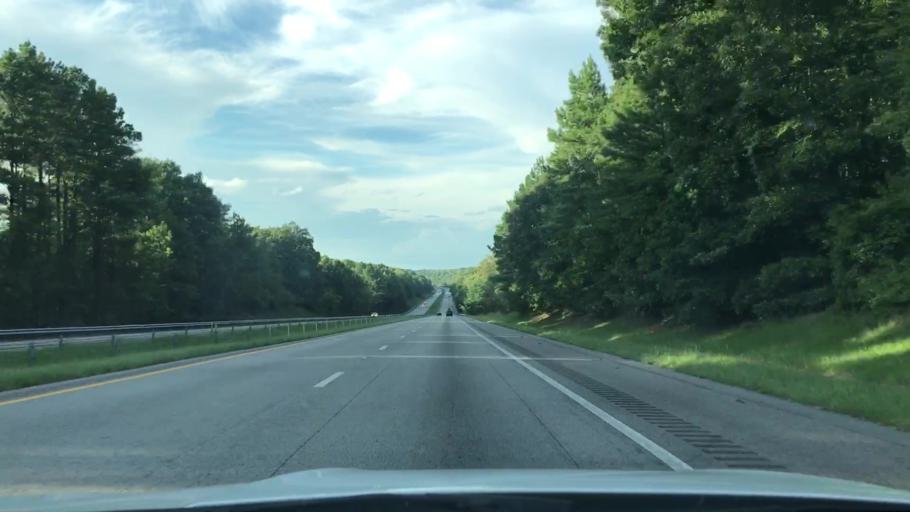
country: US
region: South Carolina
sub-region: Laurens County
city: Clinton
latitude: 34.5816
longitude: -81.8931
